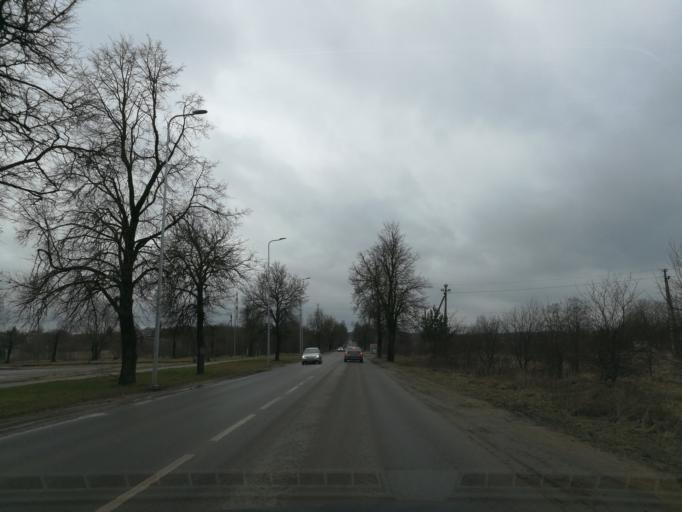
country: LT
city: Grigiskes
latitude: 54.6463
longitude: 25.1365
